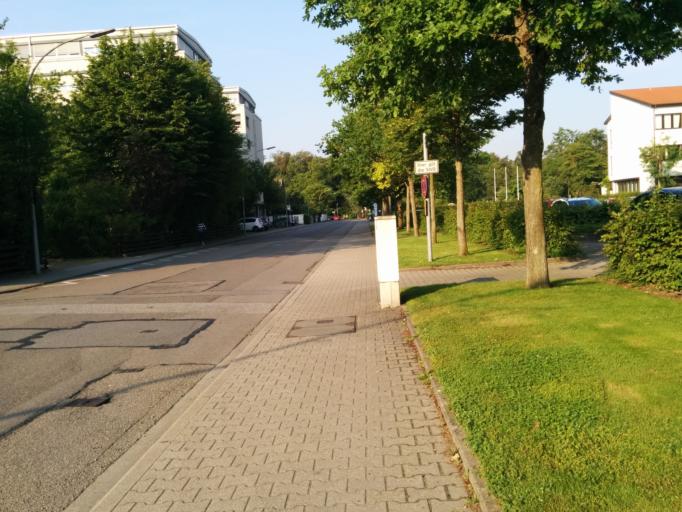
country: DE
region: Baden-Wuerttemberg
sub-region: Karlsruhe Region
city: Walldorf
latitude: 49.2925
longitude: 8.6413
